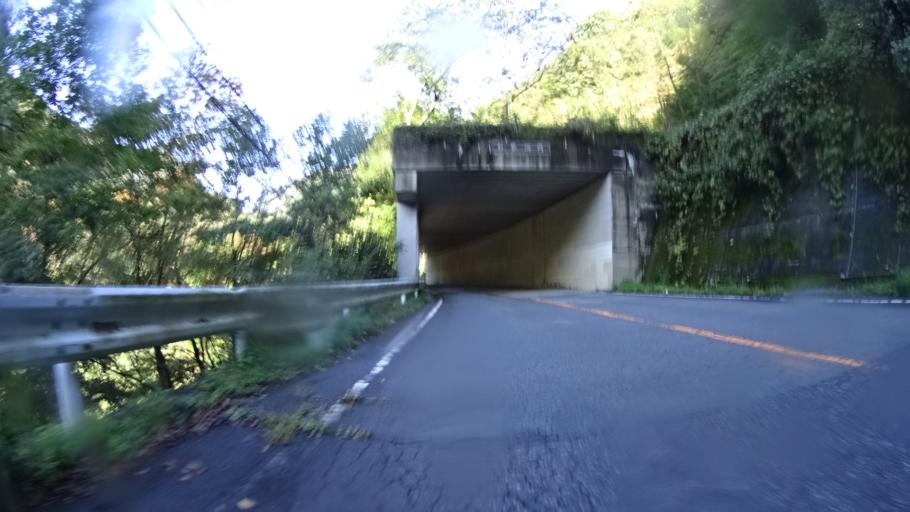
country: JP
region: Yamanashi
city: Otsuki
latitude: 35.7848
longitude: 138.9700
